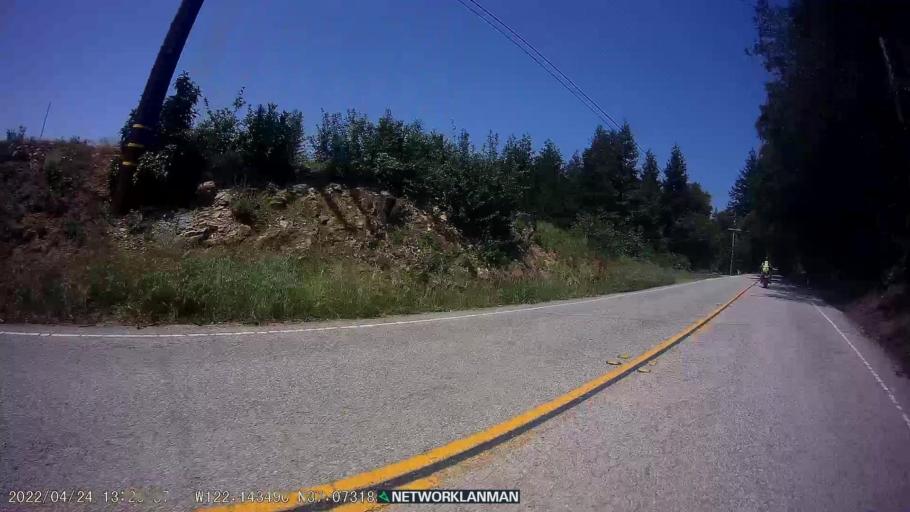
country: US
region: California
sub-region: Santa Cruz County
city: Bonny Doon
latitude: 37.0733
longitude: -122.1434
